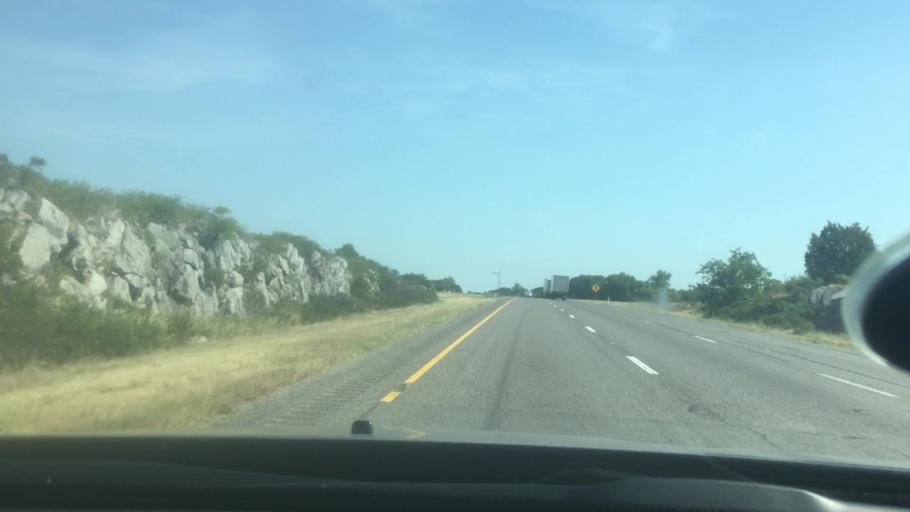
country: US
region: Oklahoma
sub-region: Murray County
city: Davis
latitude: 34.3764
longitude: -97.1442
